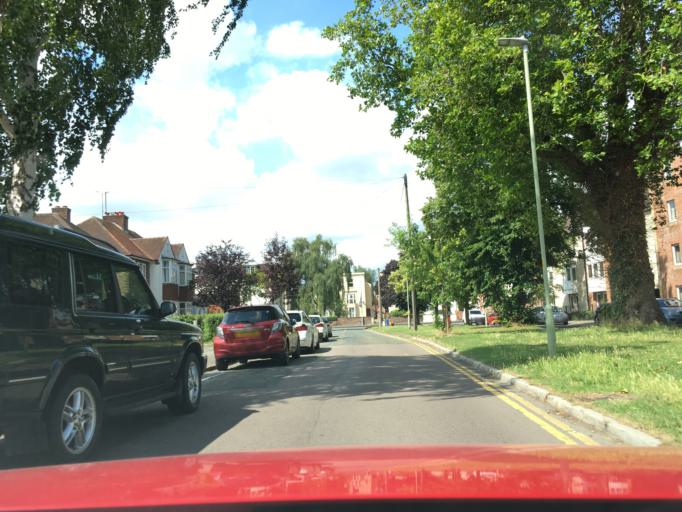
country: GB
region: England
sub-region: Gloucestershire
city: Gloucester
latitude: 51.8733
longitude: -2.2395
